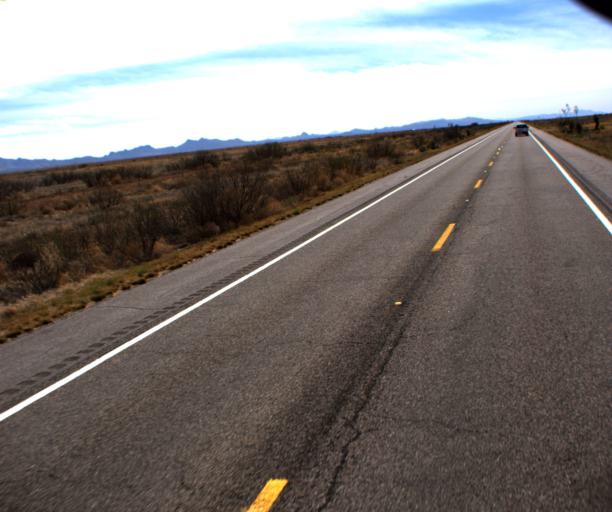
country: US
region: Arizona
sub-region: Cochise County
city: Pirtleville
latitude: 31.5192
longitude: -109.6453
